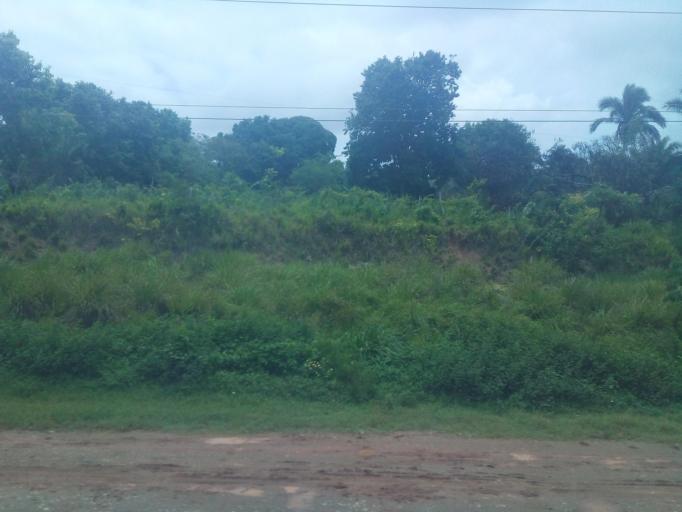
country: BR
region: Maranhao
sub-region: Vitoria Do Mearim
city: Vitoria do Mearim
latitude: -3.5945
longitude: -44.9863
